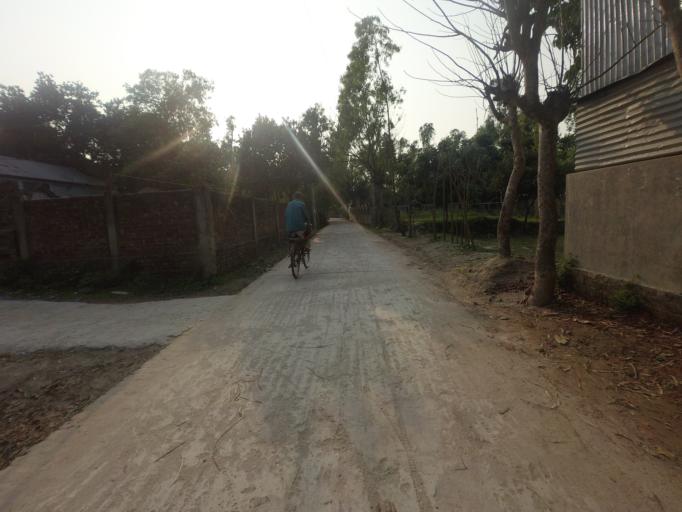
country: BD
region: Rajshahi
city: Sirajganj
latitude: 24.3234
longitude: 89.7075
